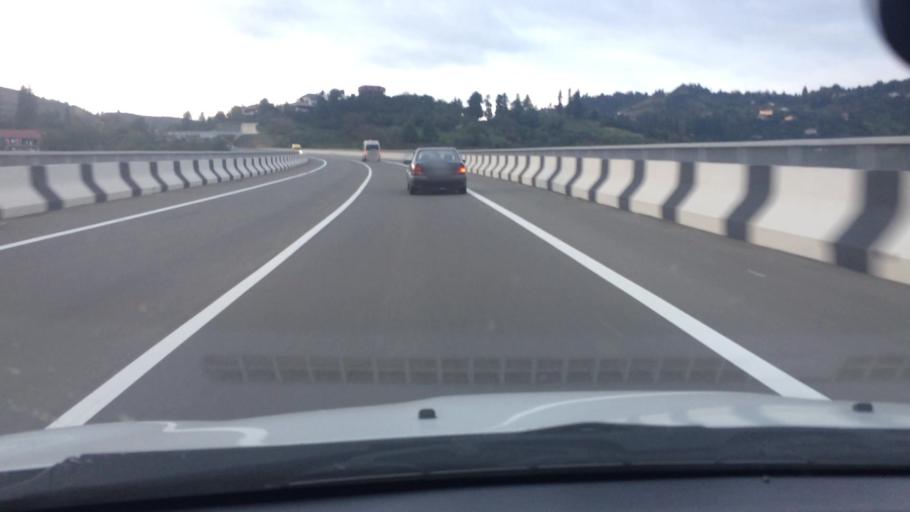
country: GE
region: Ajaria
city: Makhinjauri
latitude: 41.7147
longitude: 41.7519
